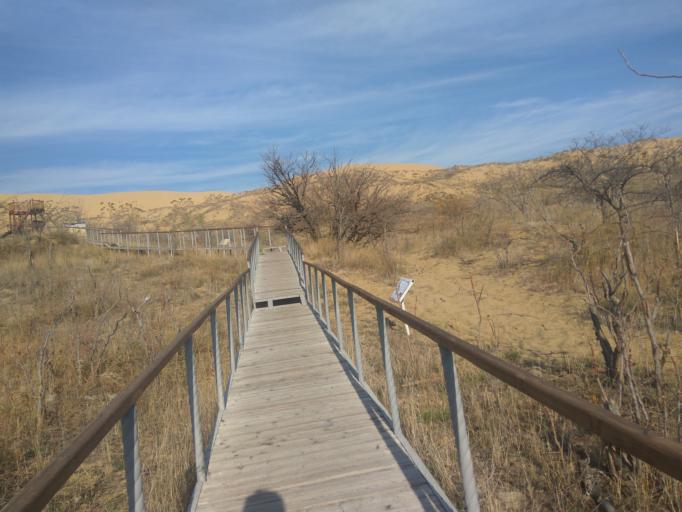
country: RU
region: Dagestan
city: Korkmaskala
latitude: 43.0036
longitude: 47.2374
